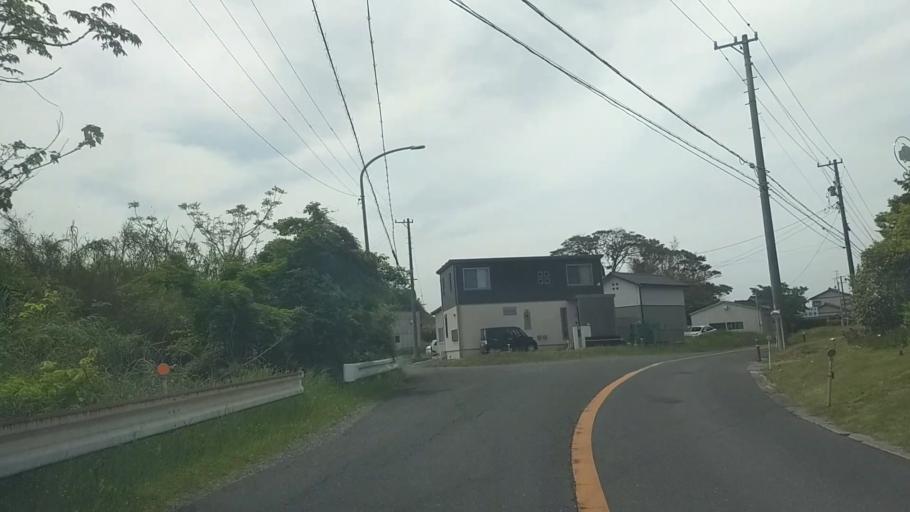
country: JP
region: Shizuoka
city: Kosai-shi
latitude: 34.7366
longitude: 137.5397
